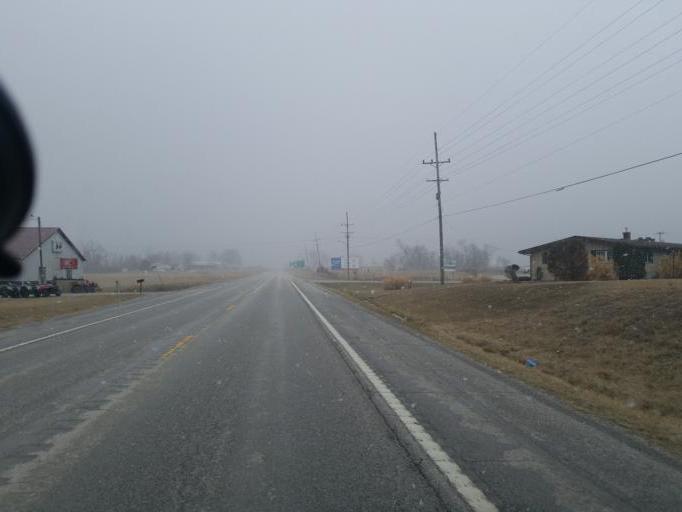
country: US
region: Missouri
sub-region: Adair County
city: Kirksville
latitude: 40.2507
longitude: -92.5826
